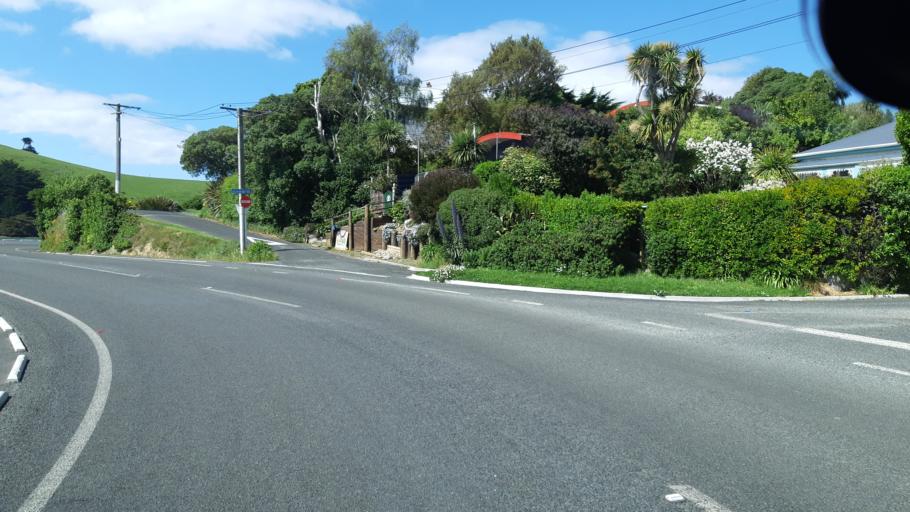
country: NZ
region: Otago
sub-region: Dunedin City
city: Portobello
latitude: -45.8384
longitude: 170.6444
